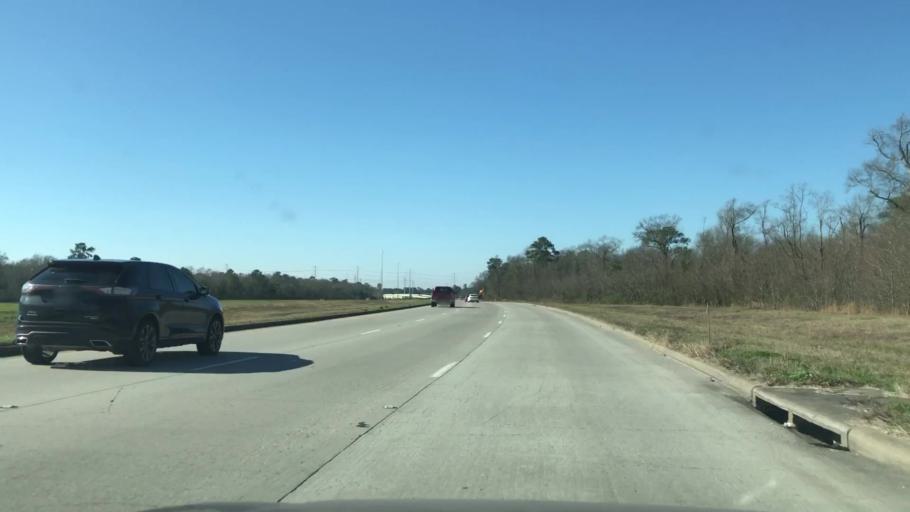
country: US
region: Texas
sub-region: Harris County
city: Cloverleaf
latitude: 29.8254
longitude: -95.1938
